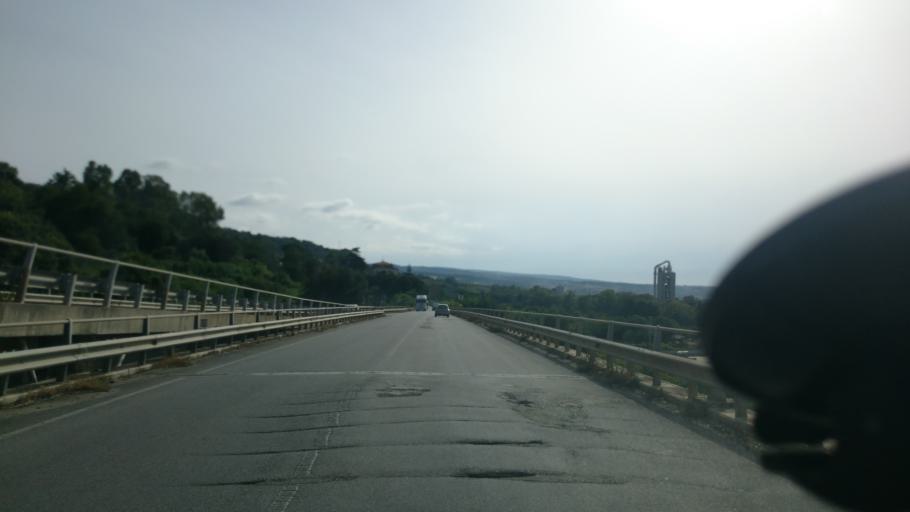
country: IT
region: Calabria
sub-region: Provincia di Vibo-Valentia
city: Sant'Onofrio
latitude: 38.7095
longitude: 16.1214
